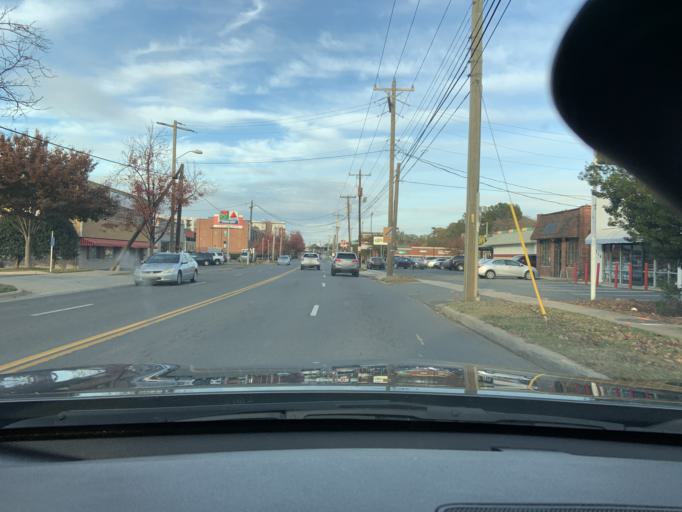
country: US
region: North Carolina
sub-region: Mecklenburg County
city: Charlotte
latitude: 35.1965
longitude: -80.8704
